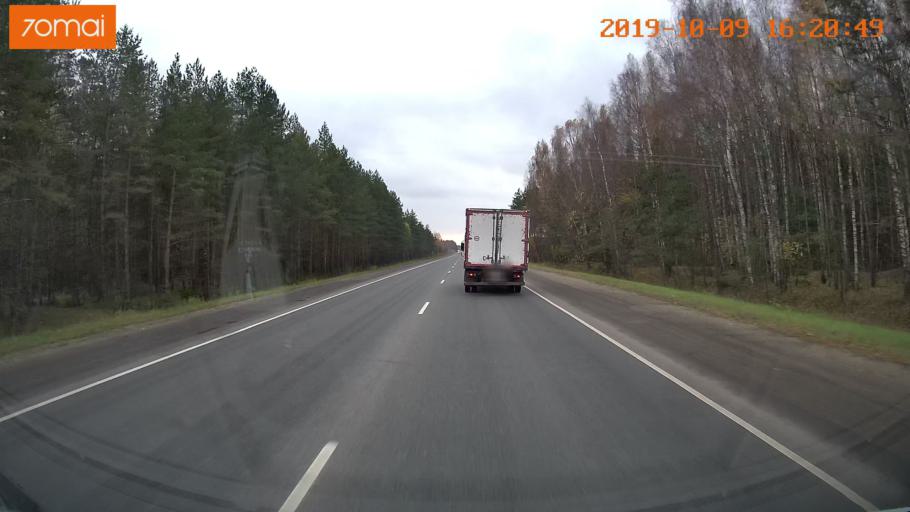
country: RU
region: Kostroma
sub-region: Kostromskoy Rayon
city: Kostroma
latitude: 57.7016
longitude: 40.8912
